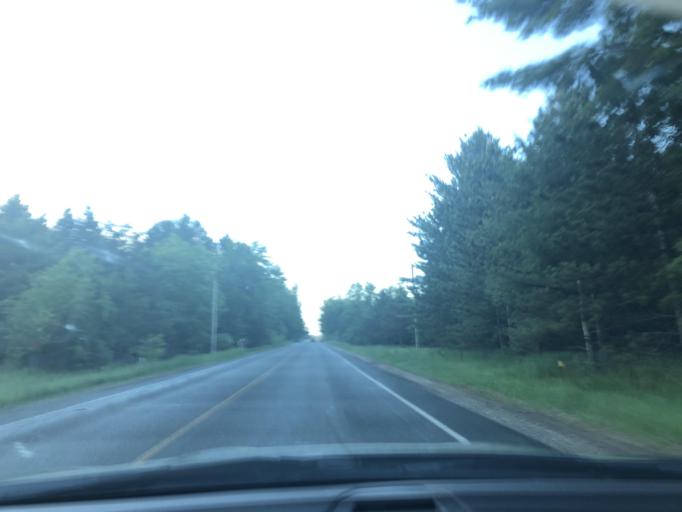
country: US
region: Michigan
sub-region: Missaukee County
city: Lake City
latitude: 44.3517
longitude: -85.0757
